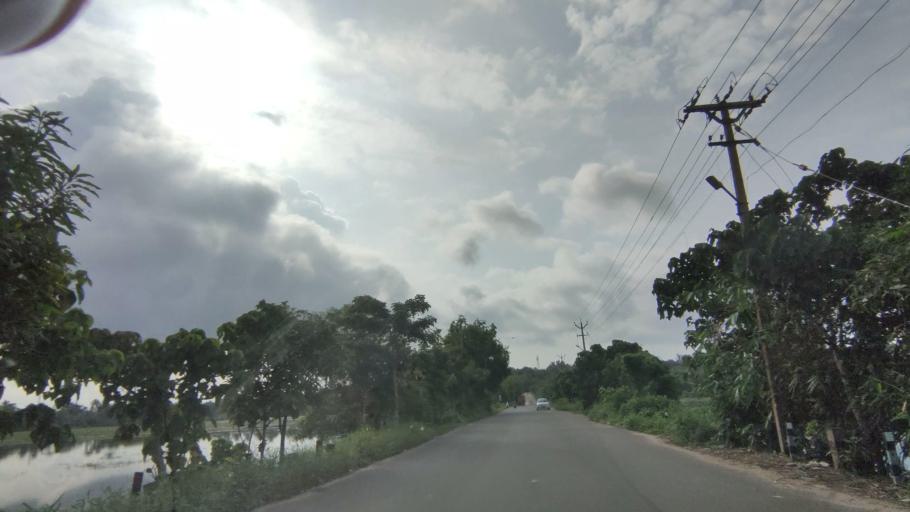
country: IN
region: Kerala
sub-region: Kottayam
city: Kottayam
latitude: 9.5644
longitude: 76.5088
